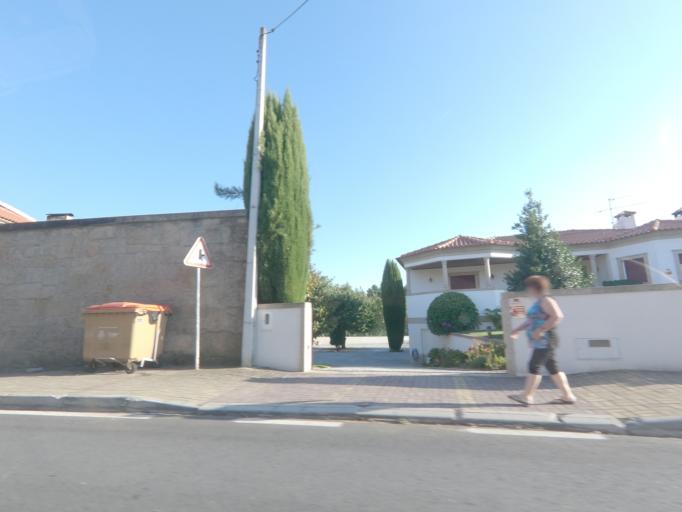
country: PT
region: Vila Real
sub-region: Vila Real
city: Vila Real
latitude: 41.2800
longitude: -7.6931
